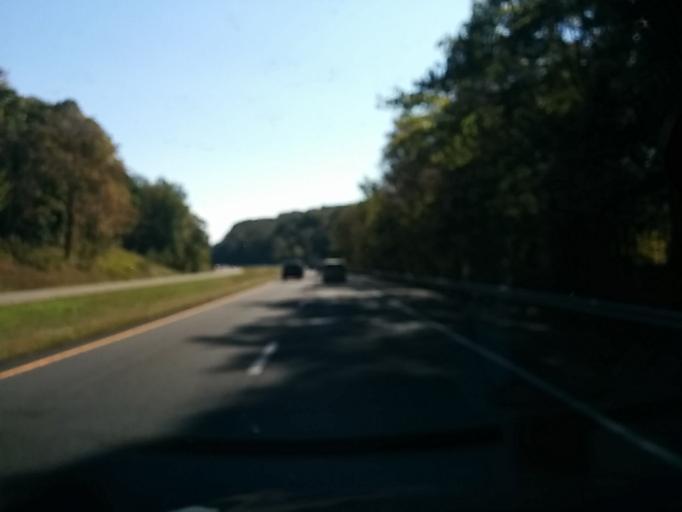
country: US
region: Virginia
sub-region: City of Charlottesville
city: Charlottesville
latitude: 38.0234
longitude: -78.5801
